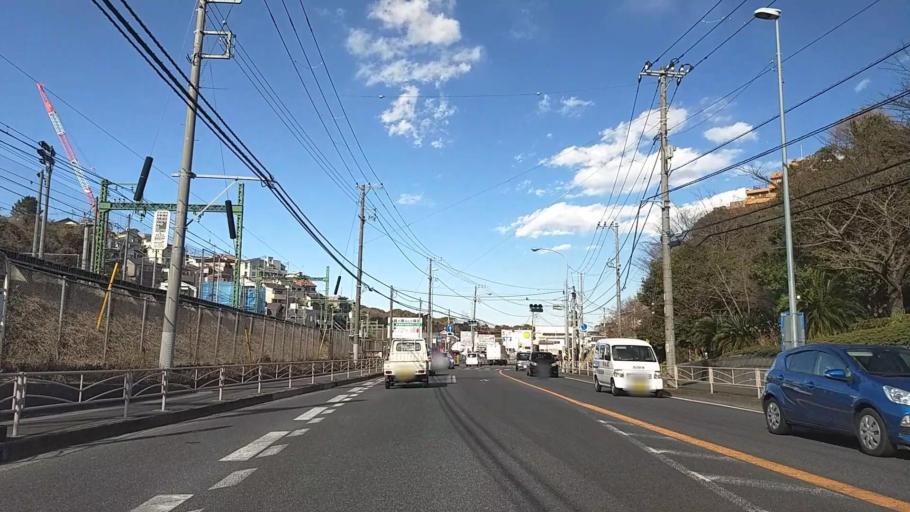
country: JP
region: Kanagawa
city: Yokohama
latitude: 35.3620
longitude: 139.6298
